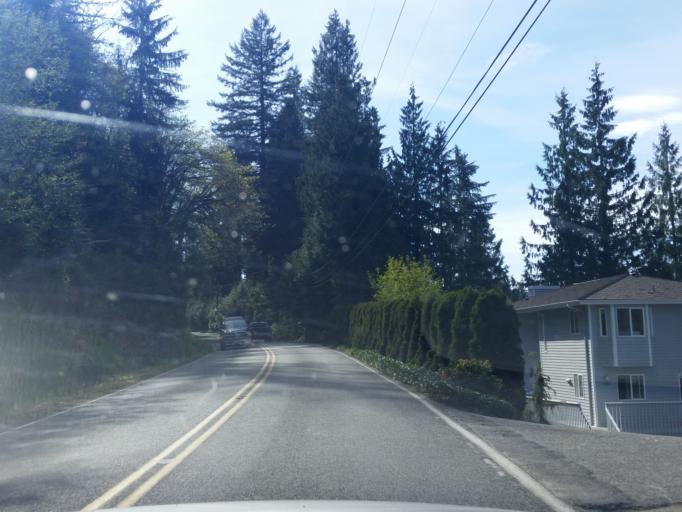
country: US
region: Washington
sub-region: Snohomish County
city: Granite Falls
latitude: 47.9901
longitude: -121.9096
